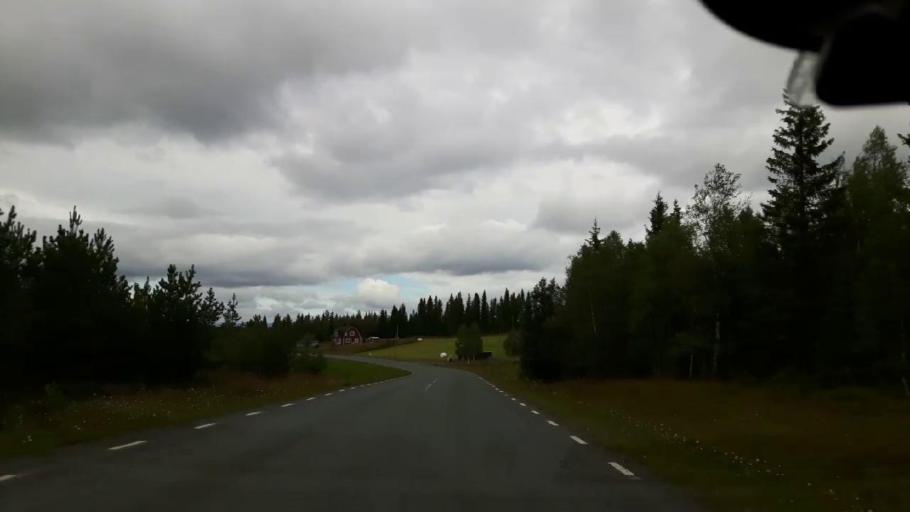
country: SE
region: Jaemtland
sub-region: Krokoms Kommun
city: Valla
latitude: 63.5414
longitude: 13.8563
